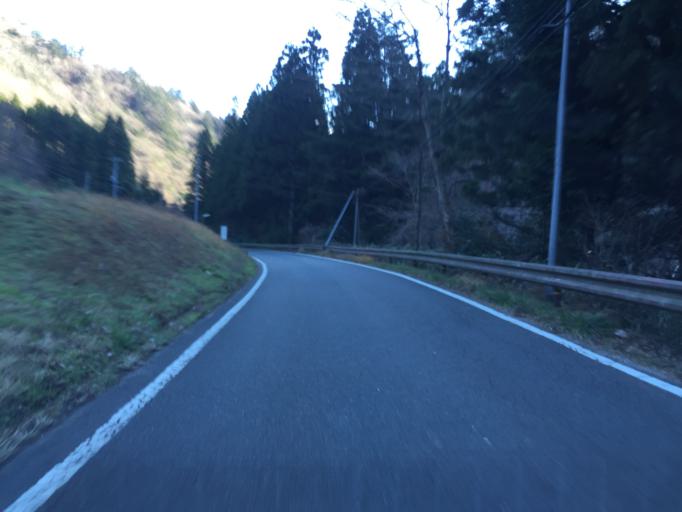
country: JP
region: Fukushima
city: Iwaki
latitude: 37.1685
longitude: 140.8258
